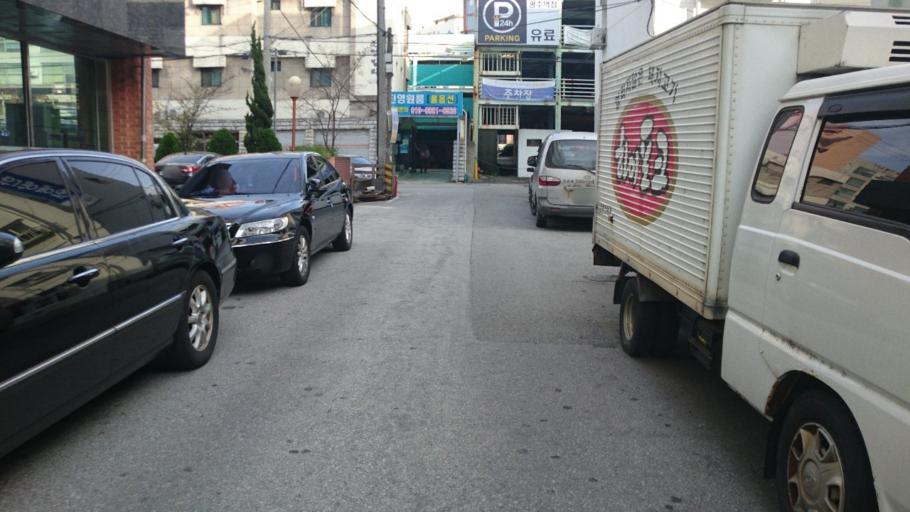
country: KR
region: Gwangju
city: Gwangju
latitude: 35.1618
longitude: 126.9078
